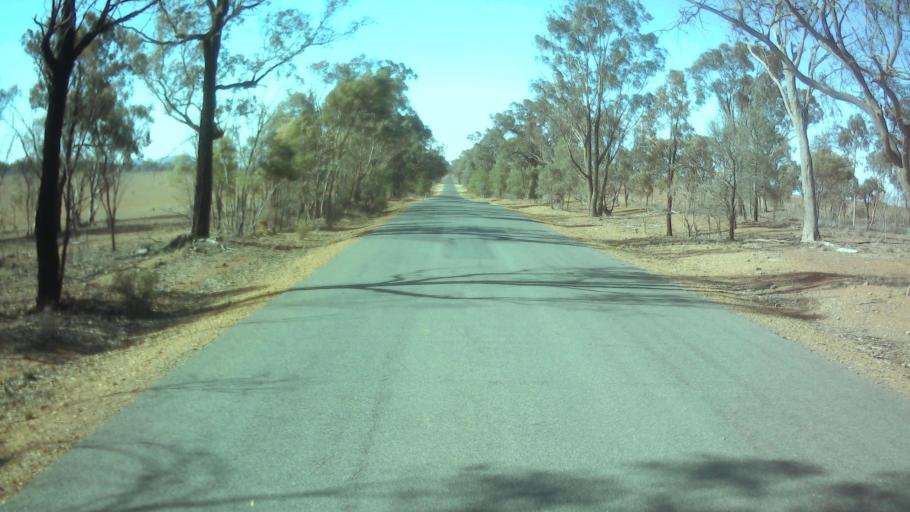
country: AU
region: New South Wales
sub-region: Forbes
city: Forbes
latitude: -33.7047
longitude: 147.8059
